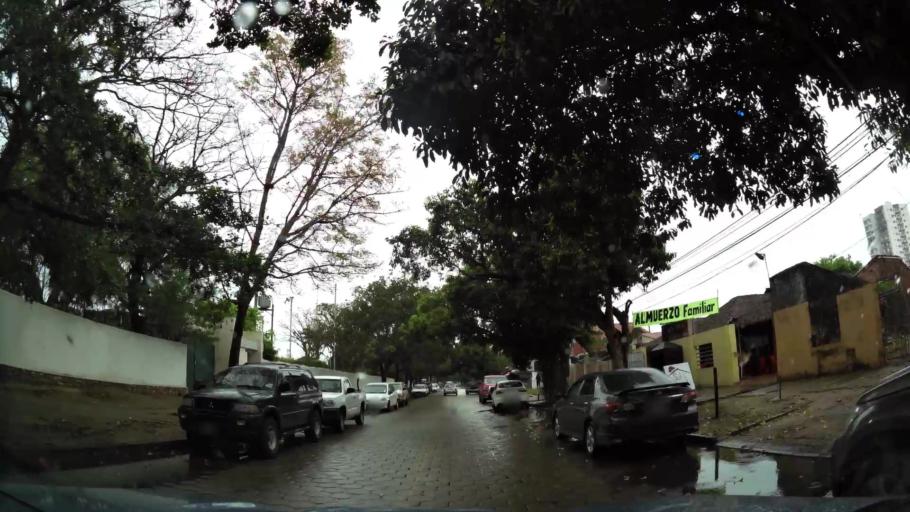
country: BO
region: Santa Cruz
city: Santa Cruz de la Sierra
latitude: -17.7814
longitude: -63.1970
